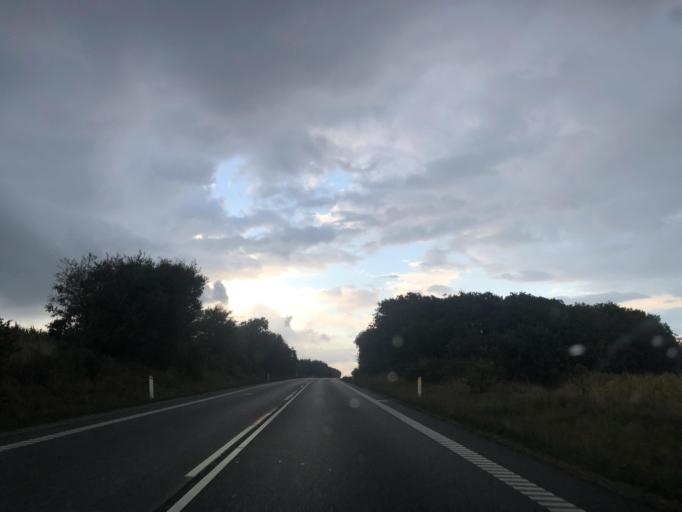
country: DK
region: Central Jutland
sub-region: Viborg Kommune
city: Stoholm
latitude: 56.4367
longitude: 9.1446
